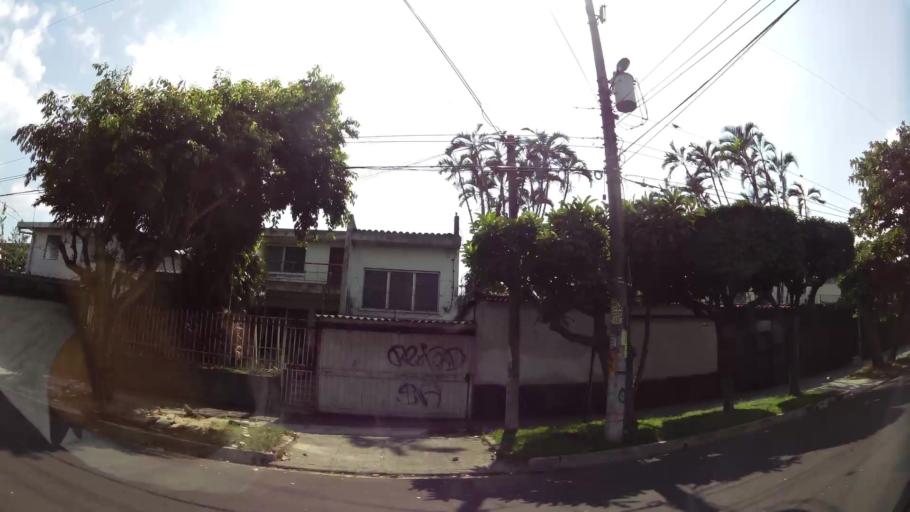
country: SV
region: San Salvador
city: Mejicanos
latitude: 13.7167
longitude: -89.2073
